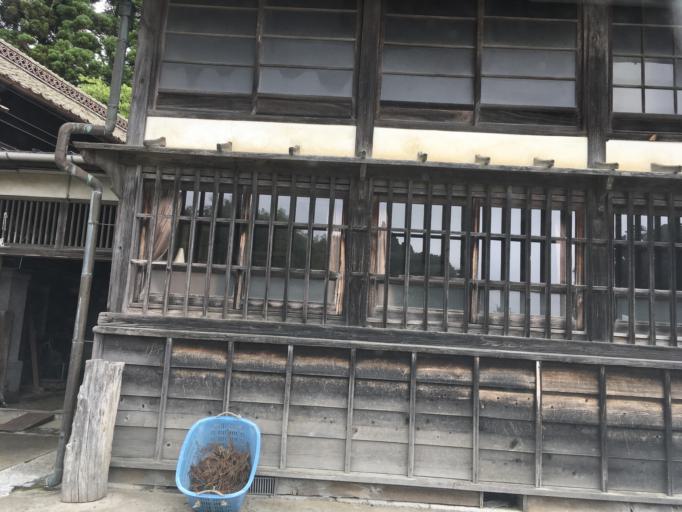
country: JP
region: Iwate
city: Ofunato
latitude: 38.8914
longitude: 141.6368
